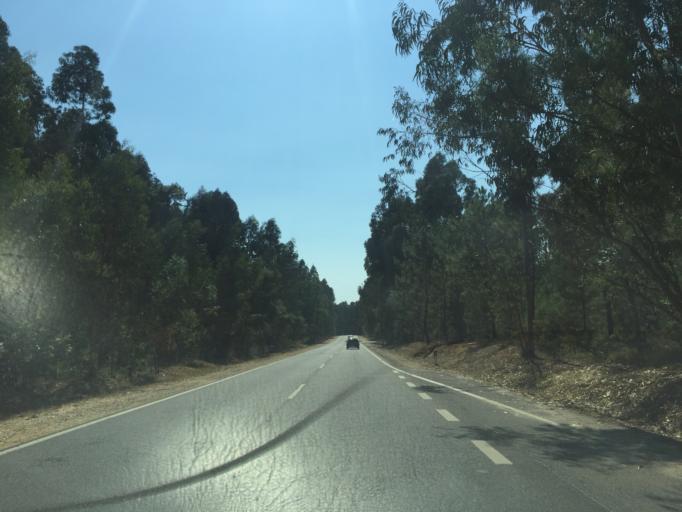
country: PT
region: Coimbra
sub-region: Cantanhede
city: Cantanhede
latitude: 40.3582
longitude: -8.5269
